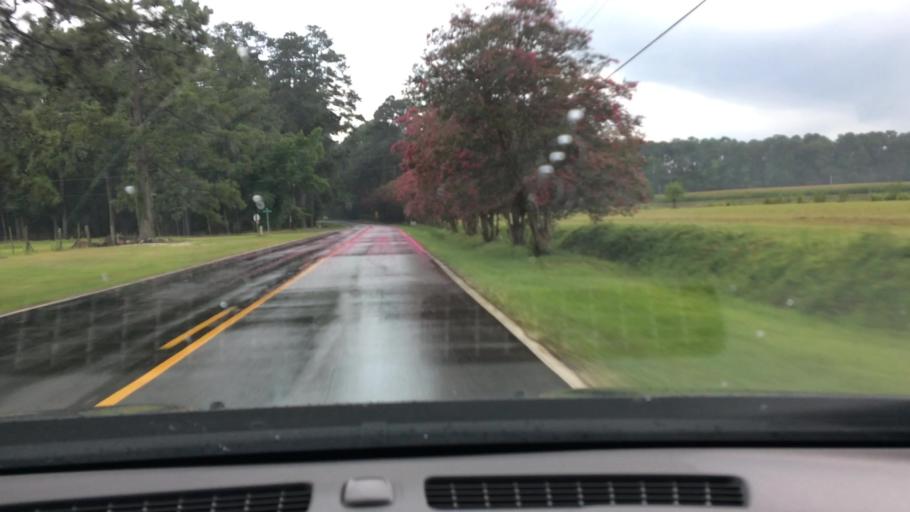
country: US
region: North Carolina
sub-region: Pitt County
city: Winterville
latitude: 35.5068
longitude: -77.3812
